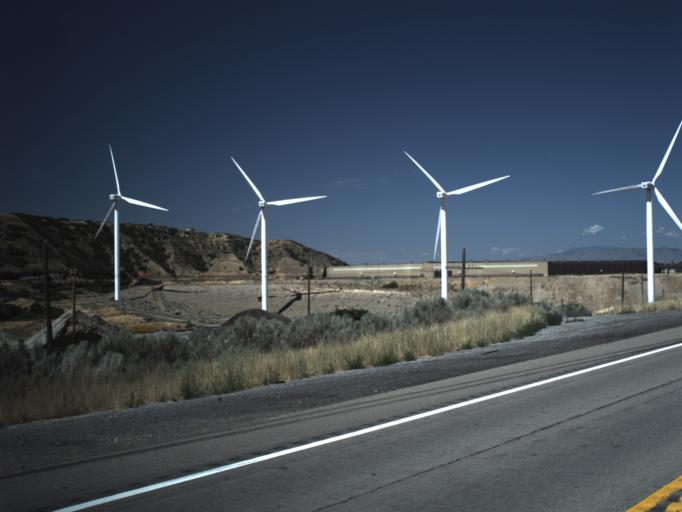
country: US
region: Utah
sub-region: Utah County
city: Mapleton
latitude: 40.0735
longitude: -111.5788
